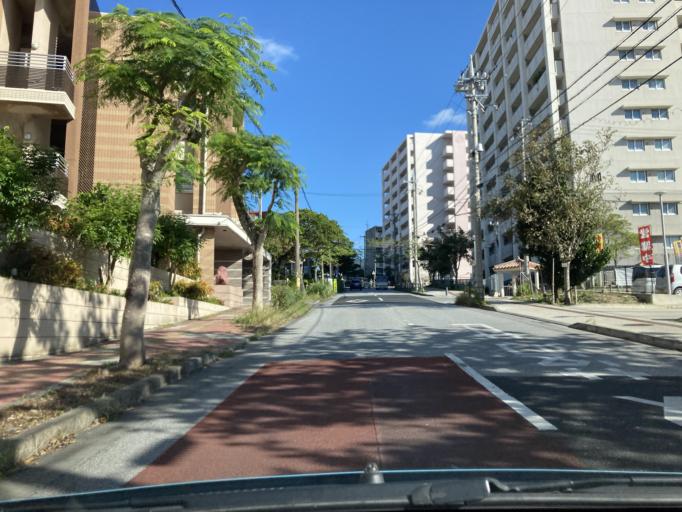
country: JP
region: Okinawa
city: Ginowan
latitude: 26.2250
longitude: 127.7321
